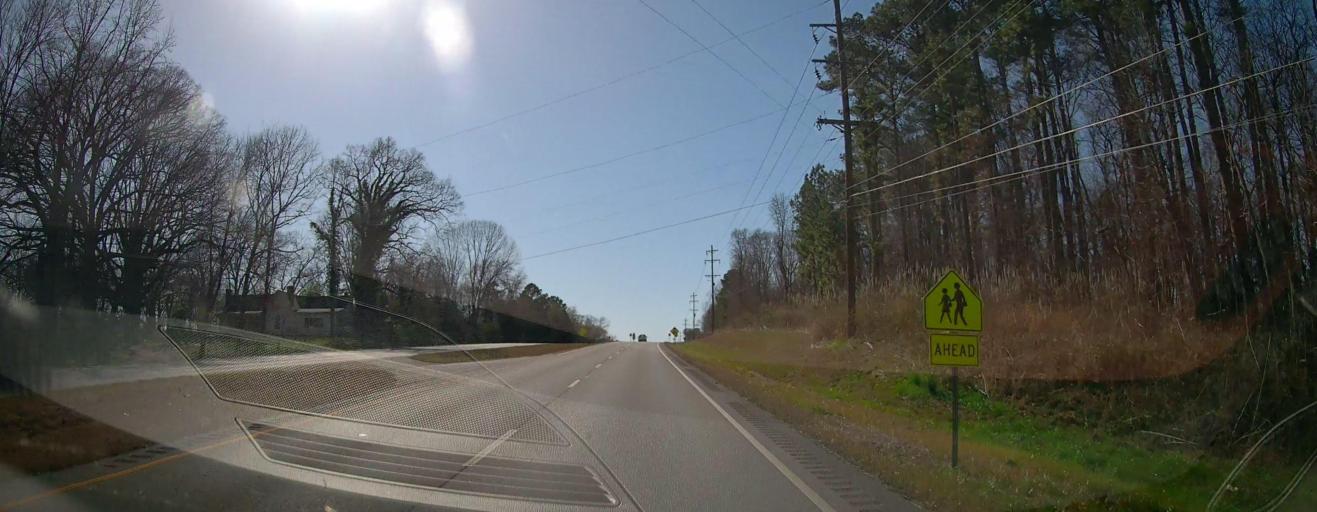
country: US
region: Alabama
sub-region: Lauderdale County
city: Killen
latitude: 34.8598
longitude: -87.4871
